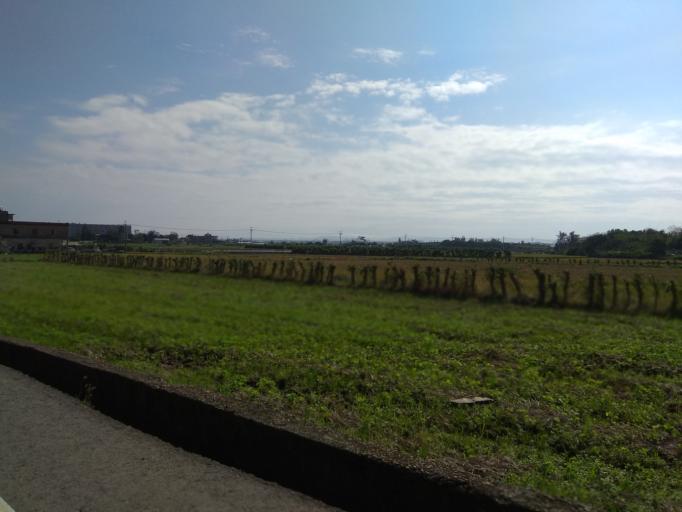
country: TW
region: Taiwan
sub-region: Hsinchu
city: Zhubei
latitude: 24.9498
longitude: 121.0127
